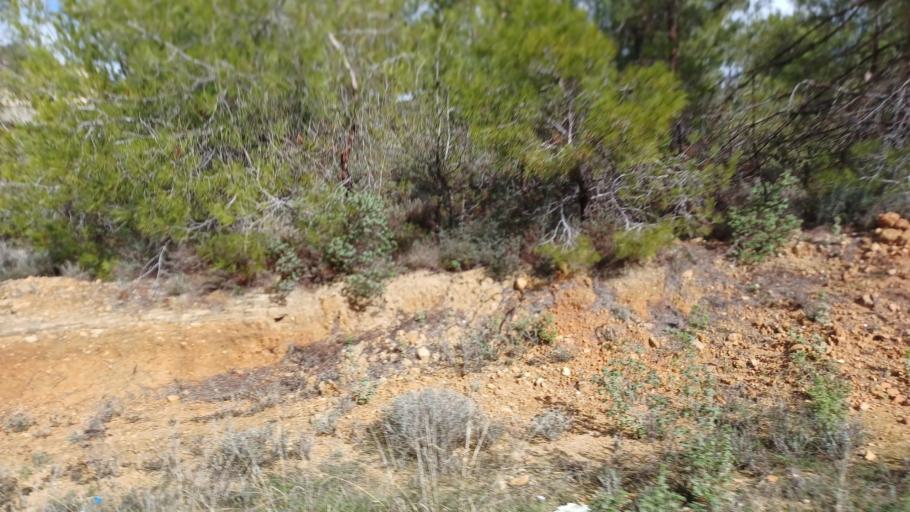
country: CY
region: Limassol
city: Sotira
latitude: 34.7093
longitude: 32.8664
